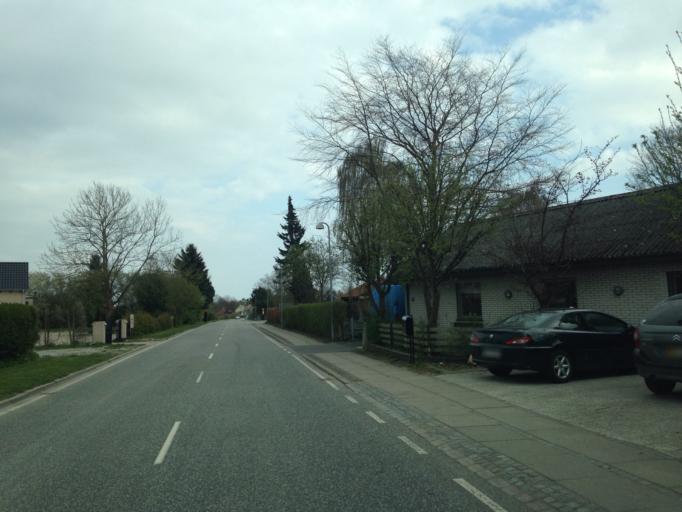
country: DK
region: Capital Region
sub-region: Hoje-Taastrup Kommune
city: Taastrup
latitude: 55.6297
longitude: 12.2856
